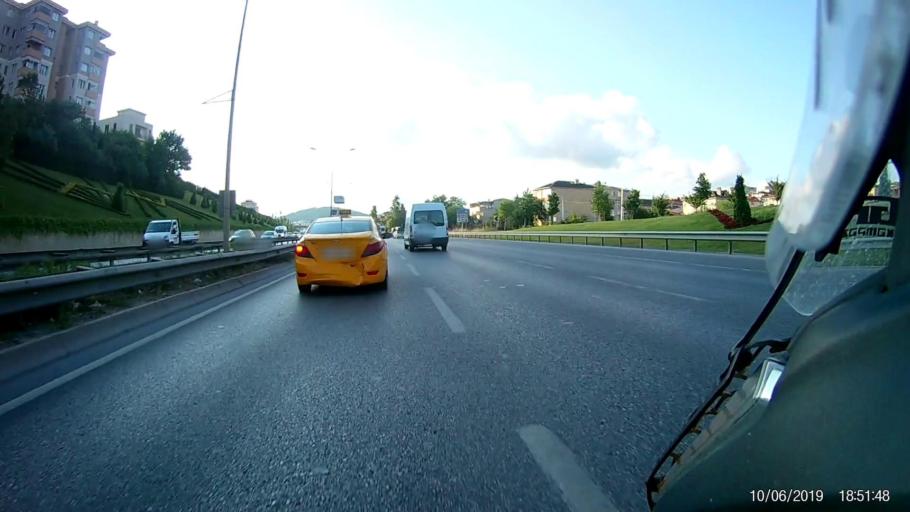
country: TR
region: Istanbul
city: Sancaktepe
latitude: 41.0344
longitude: 29.2567
